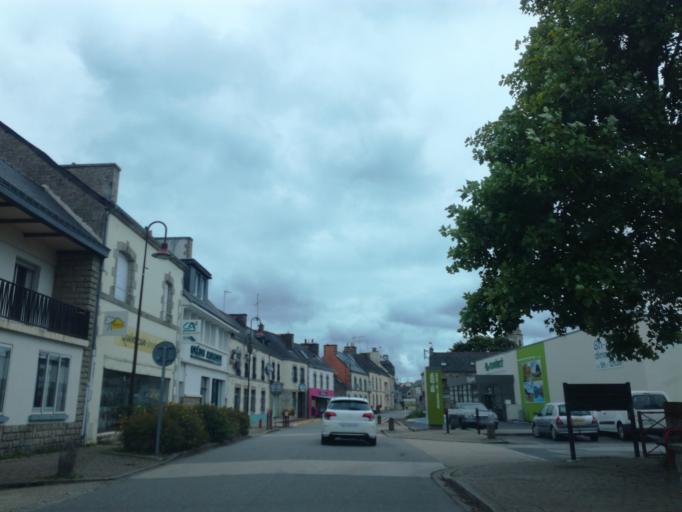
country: FR
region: Brittany
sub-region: Departement du Morbihan
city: Cleguerec
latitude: 48.1254
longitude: -3.0711
